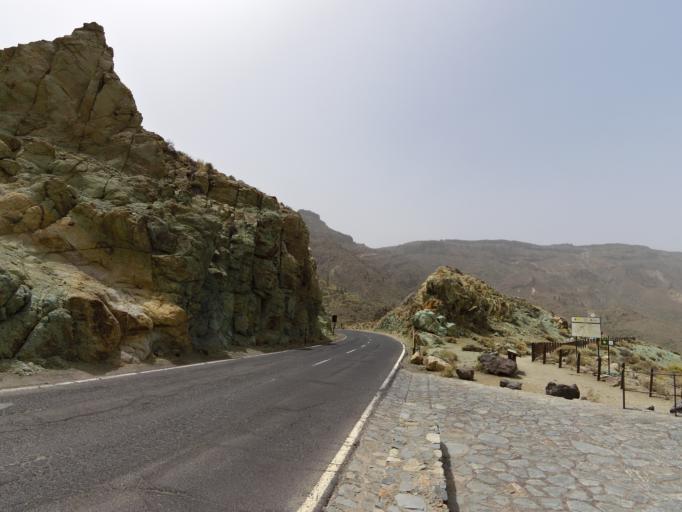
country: ES
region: Canary Islands
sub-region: Provincia de Santa Cruz de Tenerife
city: Vilaflor
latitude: 28.2187
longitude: -16.6279
